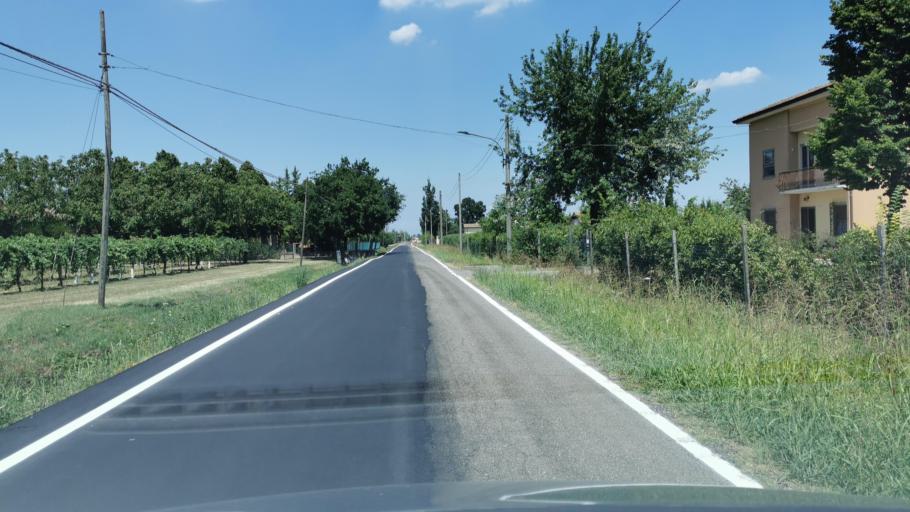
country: IT
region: Emilia-Romagna
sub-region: Provincia di Modena
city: Fossoli
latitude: 44.8247
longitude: 10.8995
